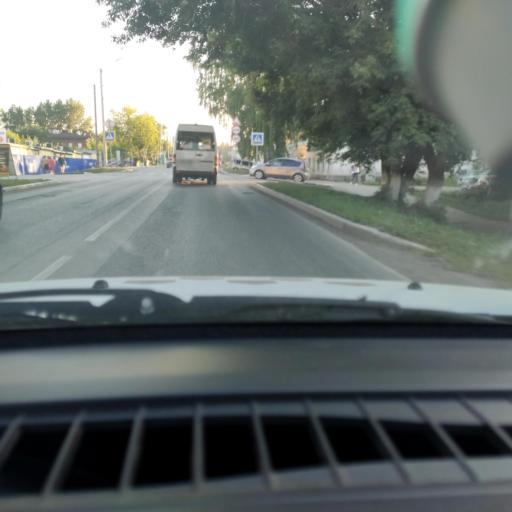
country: RU
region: Perm
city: Kungur
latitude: 57.4339
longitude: 56.9458
